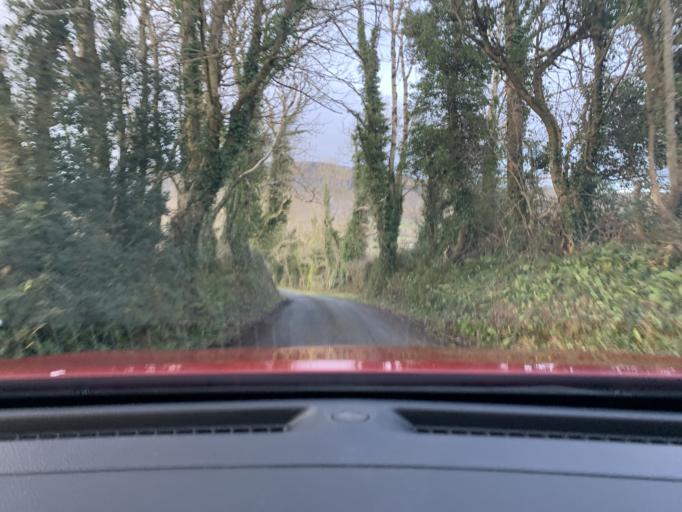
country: IE
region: Connaught
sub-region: Sligo
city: Sligo
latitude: 54.3183
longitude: -8.4481
